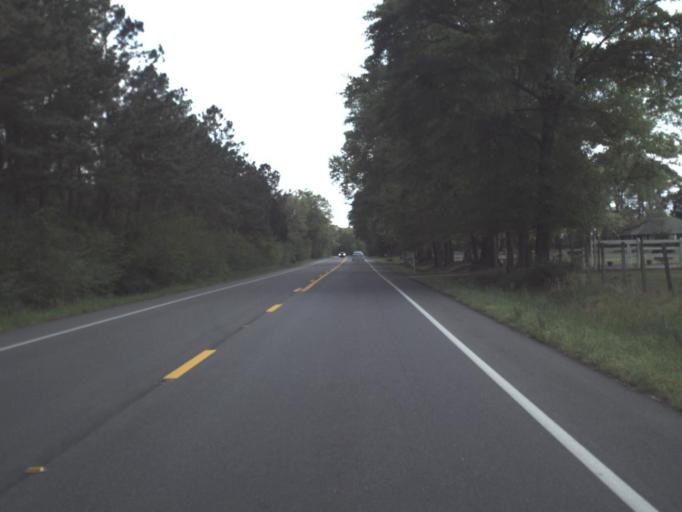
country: US
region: Alabama
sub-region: Covington County
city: Florala
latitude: 30.9463
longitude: -86.4777
